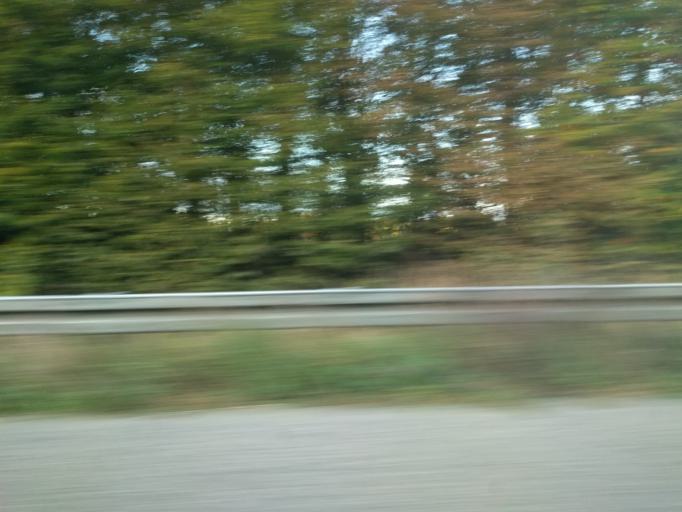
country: DK
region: South Denmark
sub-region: Nyborg Kommune
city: Ullerslev
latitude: 55.3470
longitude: 10.6376
